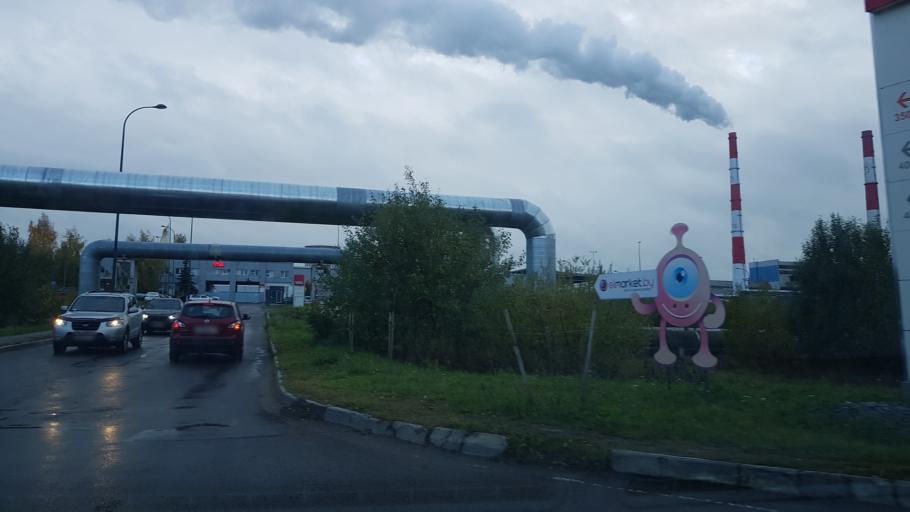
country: BY
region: Minsk
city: Malinovka
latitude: 53.8777
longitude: 27.4100
